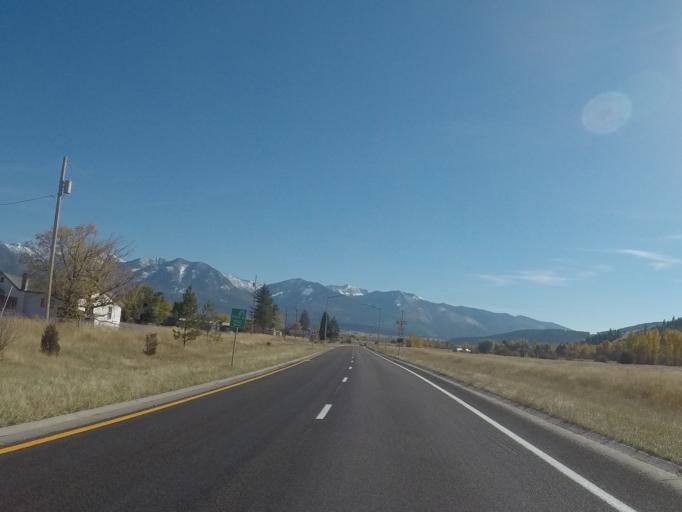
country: US
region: Montana
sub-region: Missoula County
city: Frenchtown
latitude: 47.1641
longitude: -114.0898
